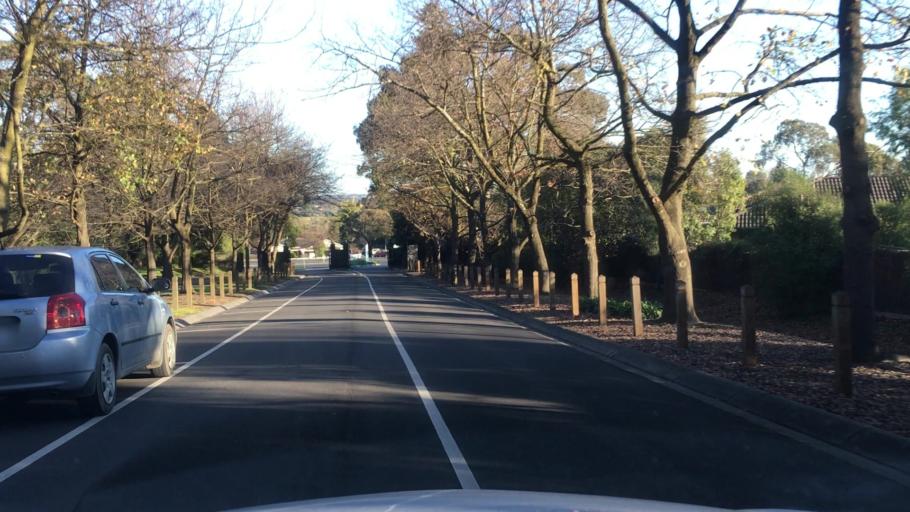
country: AU
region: Victoria
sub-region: Casey
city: Berwick
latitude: -38.0289
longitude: 145.3363
